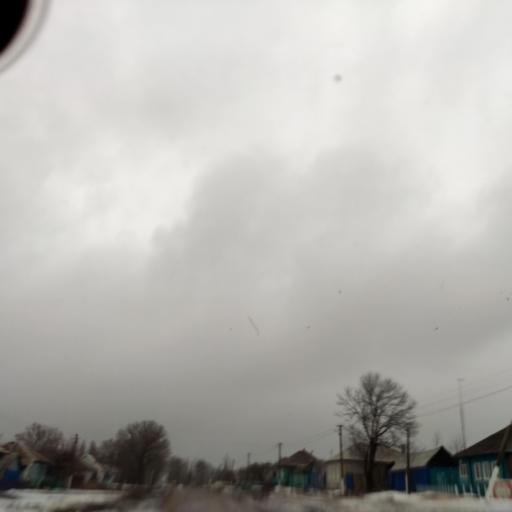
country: RU
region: Voronezj
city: Rossosh'
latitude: 51.2071
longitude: 38.7623
